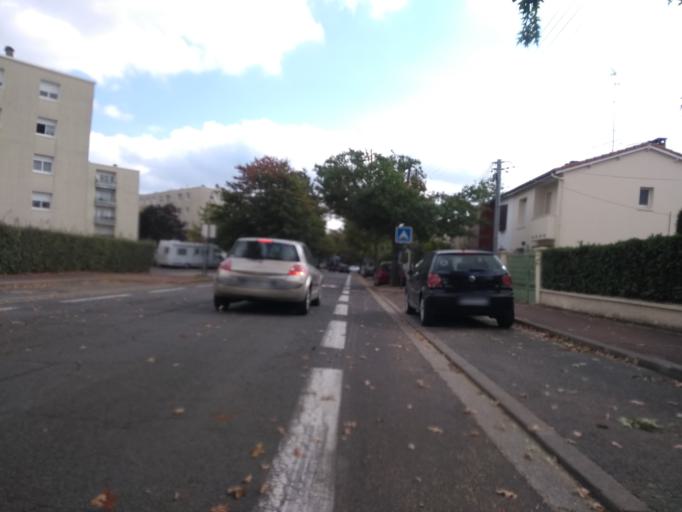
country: FR
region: Aquitaine
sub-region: Departement de la Gironde
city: Talence
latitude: 44.7922
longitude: -0.6035
